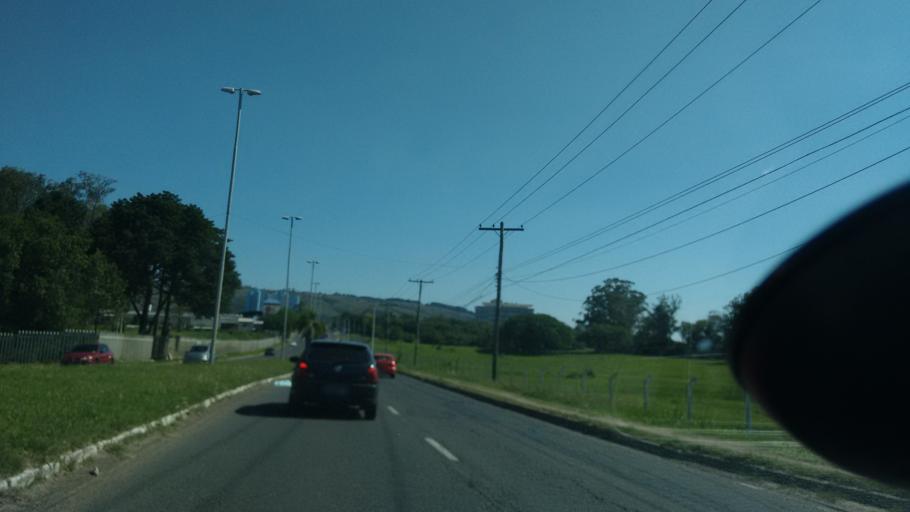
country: BR
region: Rio Grande do Sul
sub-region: Cachoeirinha
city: Cachoeirinha
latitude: -30.0274
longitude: -51.1203
